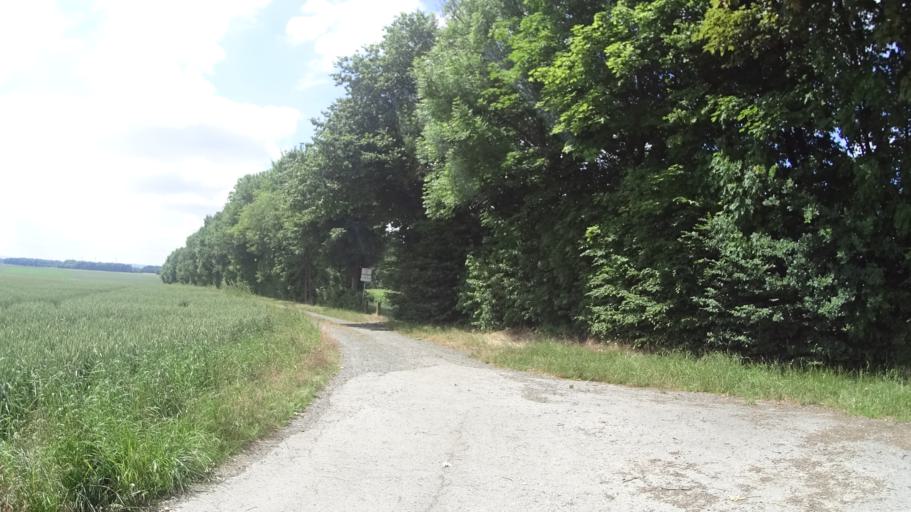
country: DE
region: Lower Saxony
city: Algermissen
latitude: 52.2402
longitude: 9.9481
